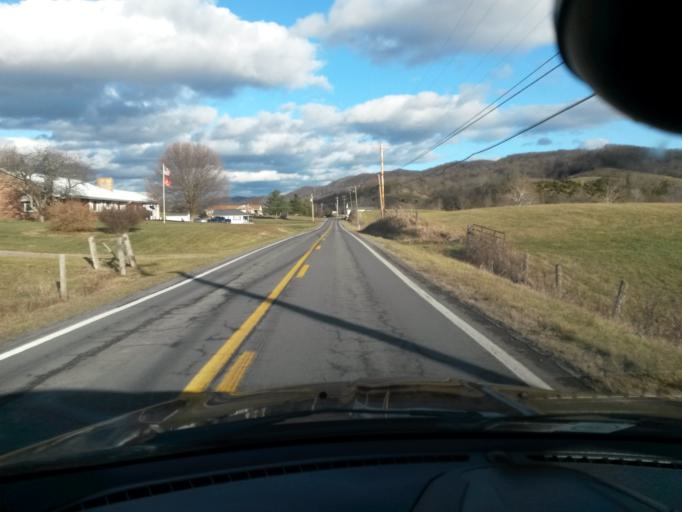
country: US
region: Virginia
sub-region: Giles County
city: Pearisburg
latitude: 37.4328
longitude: -80.7080
